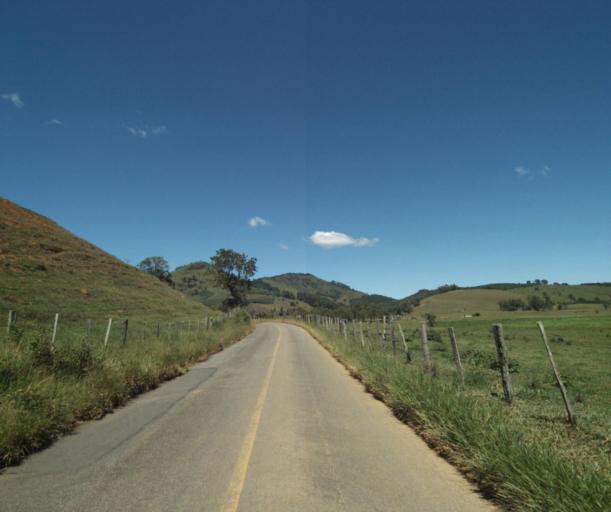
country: BR
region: Minas Gerais
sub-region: Espera Feliz
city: Espera Feliz
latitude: -20.6193
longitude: -41.8354
